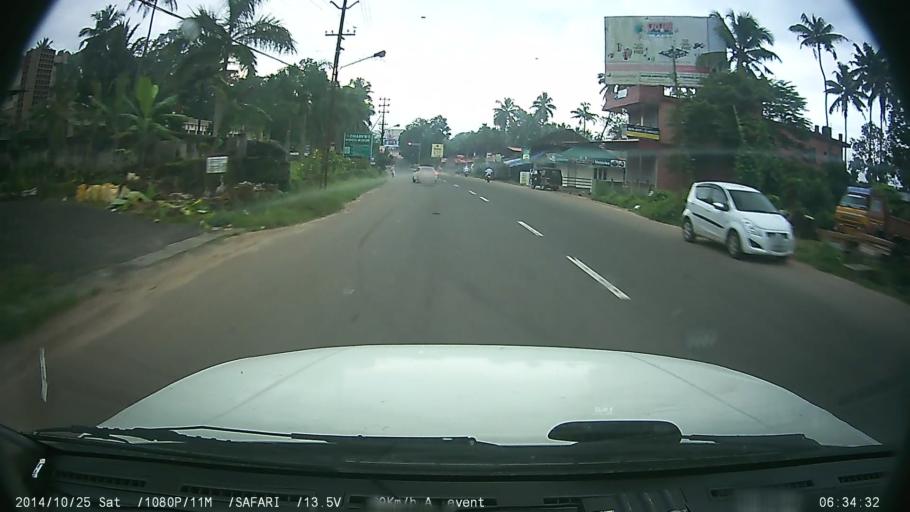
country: IN
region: Kerala
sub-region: Ernakulam
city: Muvattupula
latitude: 10.0082
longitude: 76.5689
